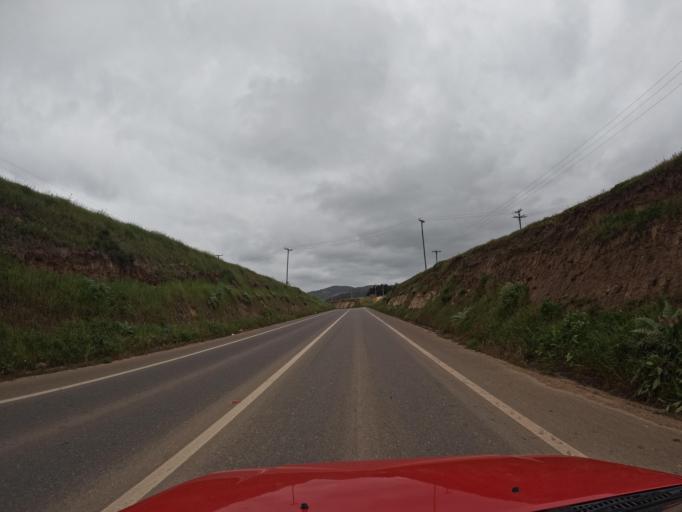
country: CL
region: O'Higgins
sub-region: Provincia de Colchagua
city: Santa Cruz
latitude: -34.4866
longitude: -72.0192
